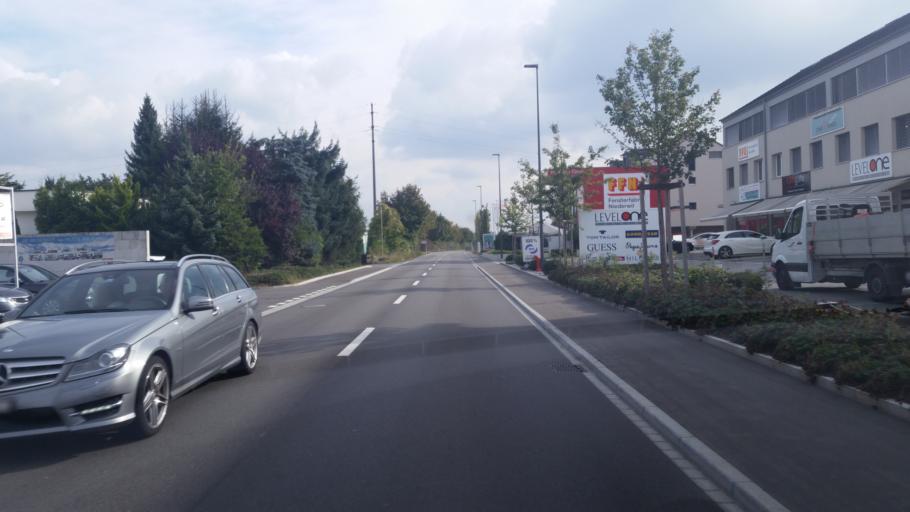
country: CH
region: Aargau
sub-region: Bezirk Baden
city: Kunten
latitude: 47.3885
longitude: 8.2947
